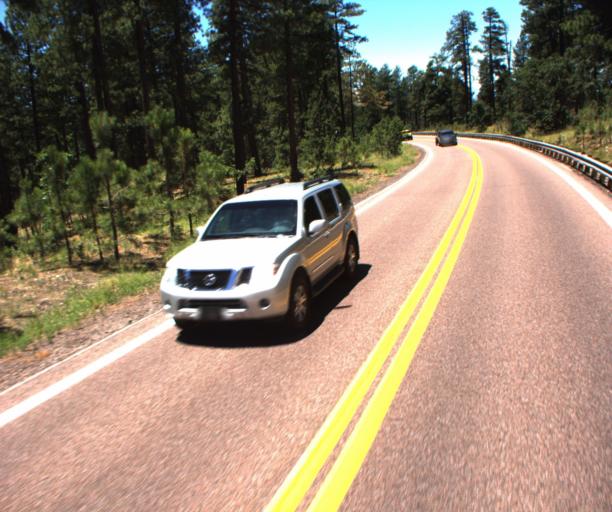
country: US
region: Arizona
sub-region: Gila County
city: Pine
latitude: 34.4434
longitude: -111.4619
